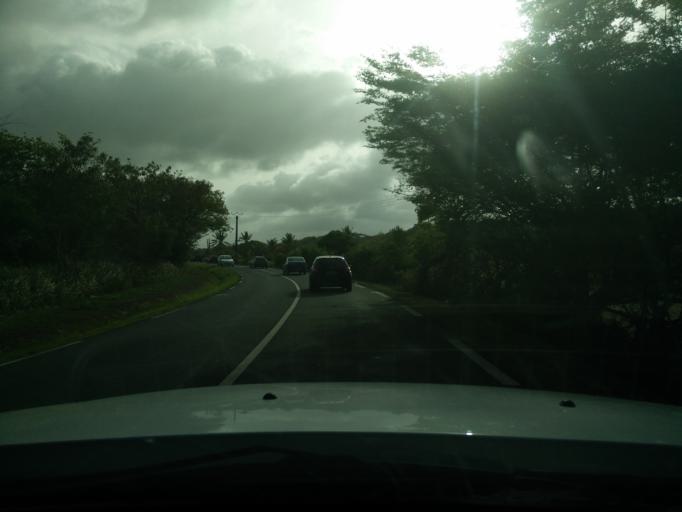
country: GP
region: Guadeloupe
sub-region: Guadeloupe
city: Saint-Francois
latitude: 16.2586
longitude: -61.3032
